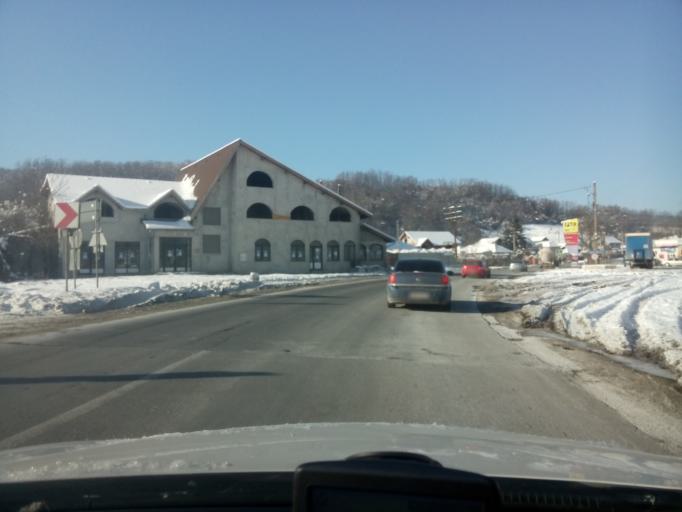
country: RO
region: Valcea
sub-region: Comuna Milcoiu
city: Milcoiu
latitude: 45.0262
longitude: 24.4841
